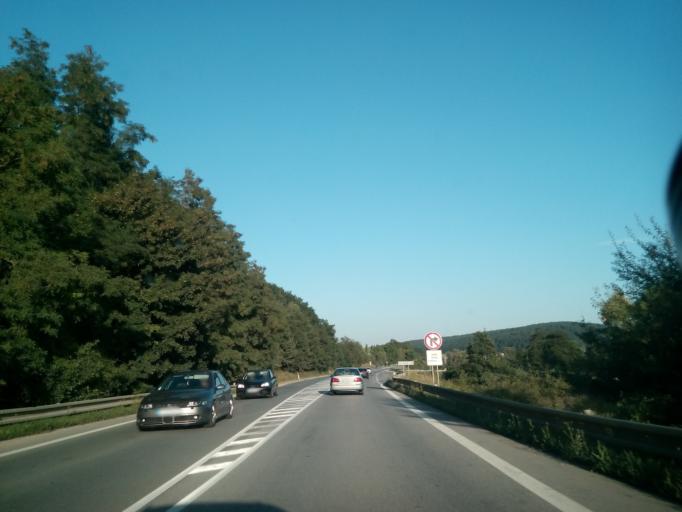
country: SK
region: Presovsky
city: Sabinov
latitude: 49.0095
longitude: 21.0632
